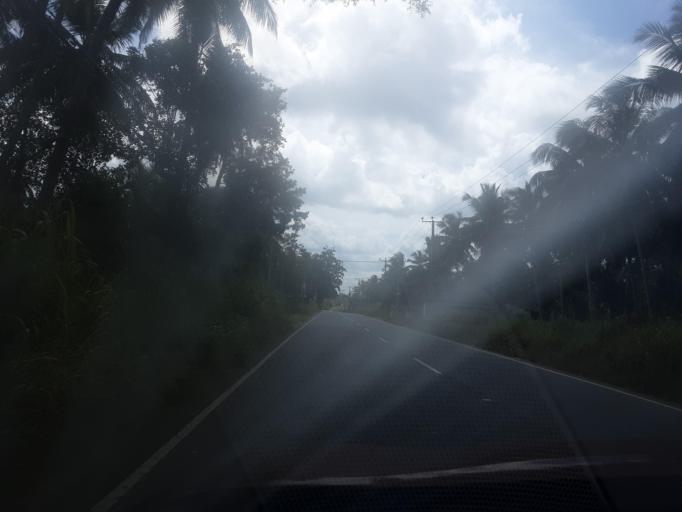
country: LK
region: North Western
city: Kuliyapitiya
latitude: 7.4780
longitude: 80.0022
